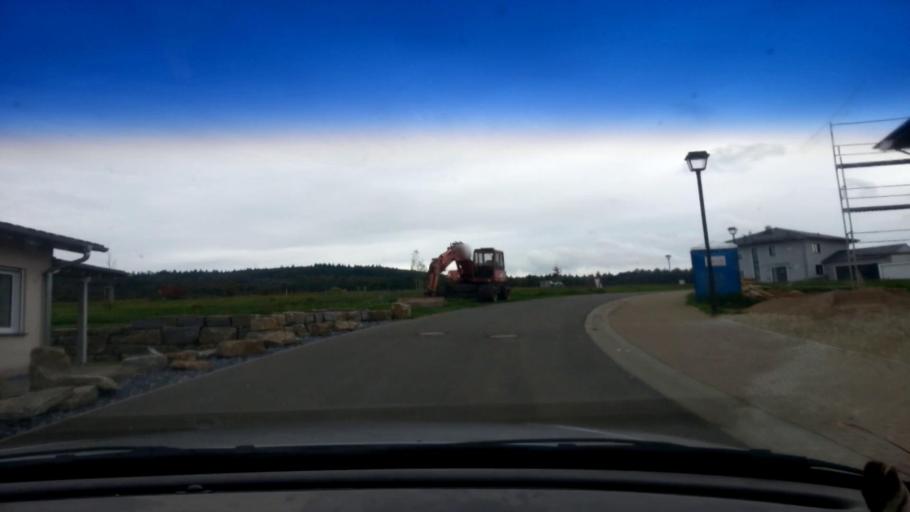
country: DE
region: Bavaria
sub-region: Upper Franconia
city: Gerach
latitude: 50.0279
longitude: 10.8030
